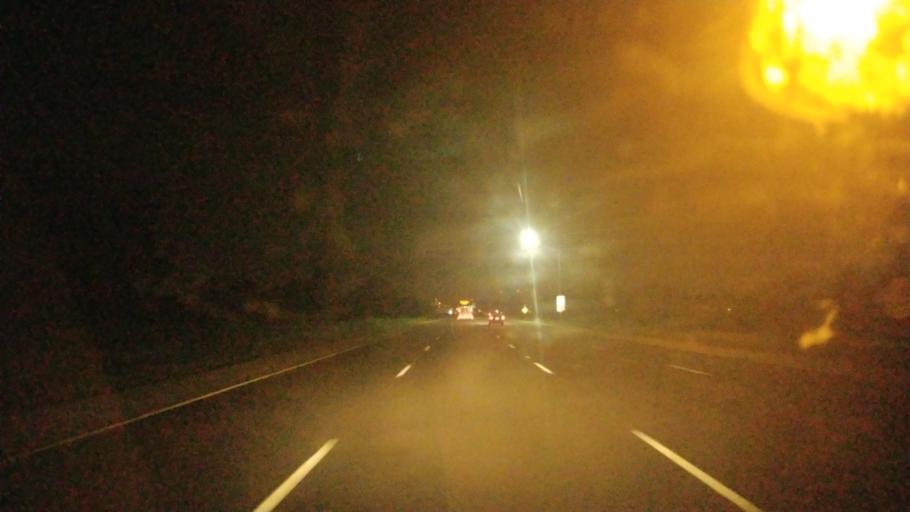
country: US
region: Illinois
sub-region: Madison County
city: Glen Carbon
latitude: 38.7568
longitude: -90.0174
